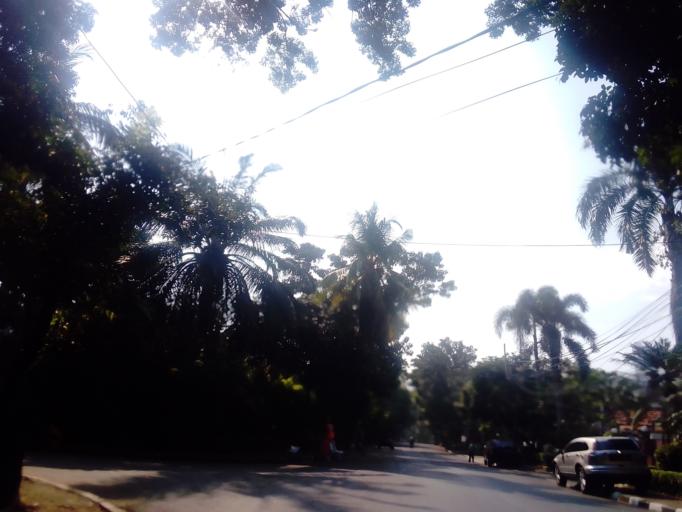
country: ID
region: Jakarta Raya
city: Jakarta
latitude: -6.2562
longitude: 106.8037
